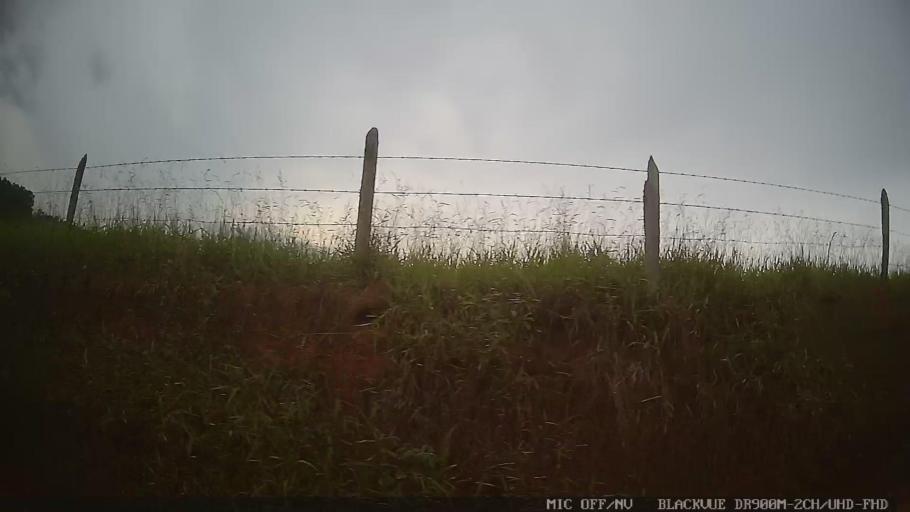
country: BR
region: Sao Paulo
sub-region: Atibaia
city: Atibaia
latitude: -23.1738
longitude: -46.5879
